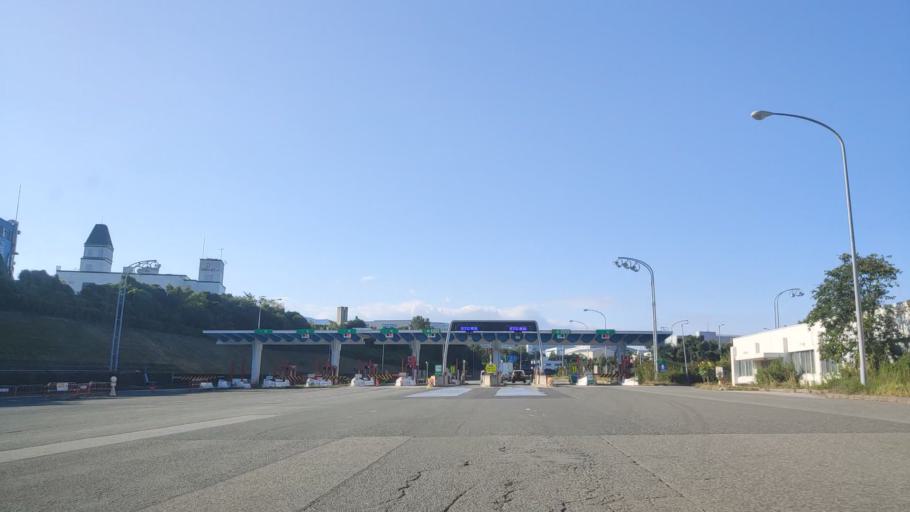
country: JP
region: Hyogo
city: Sandacho
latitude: 34.8370
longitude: 135.2354
